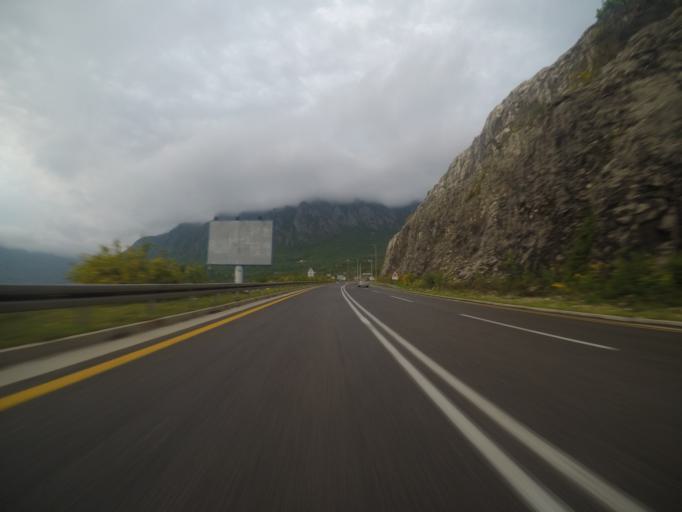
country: ME
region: Bar
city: Sutomore
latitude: 42.2062
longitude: 19.0501
